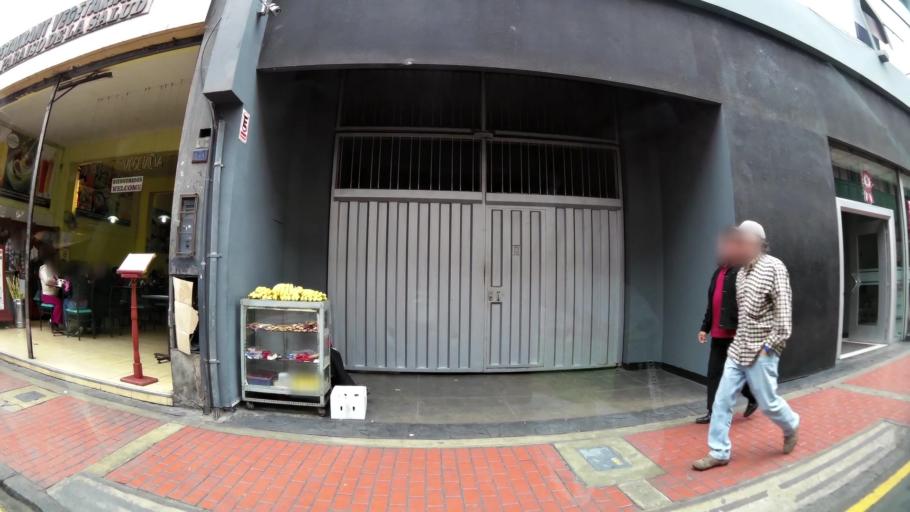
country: PE
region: Lima
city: Lima
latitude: -12.0457
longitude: -77.0326
